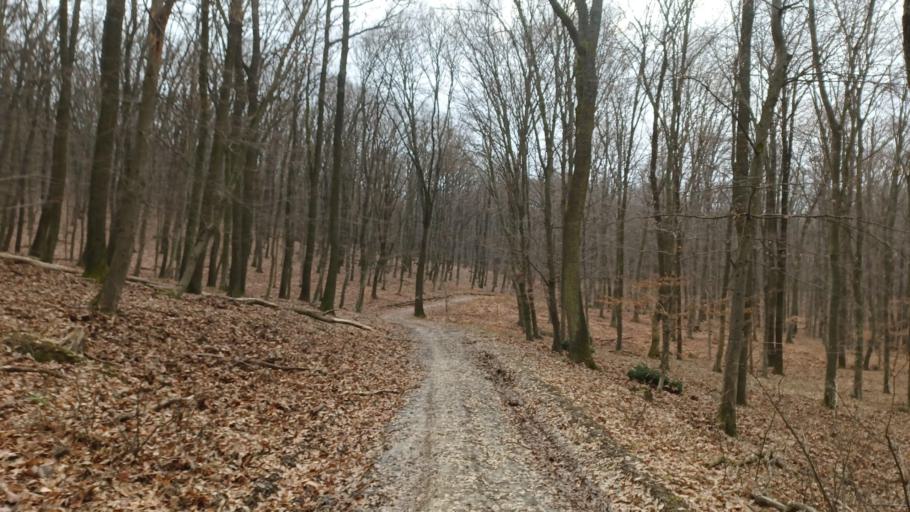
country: HU
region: Tolna
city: Szentgalpuszta
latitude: 46.3155
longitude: 18.6470
